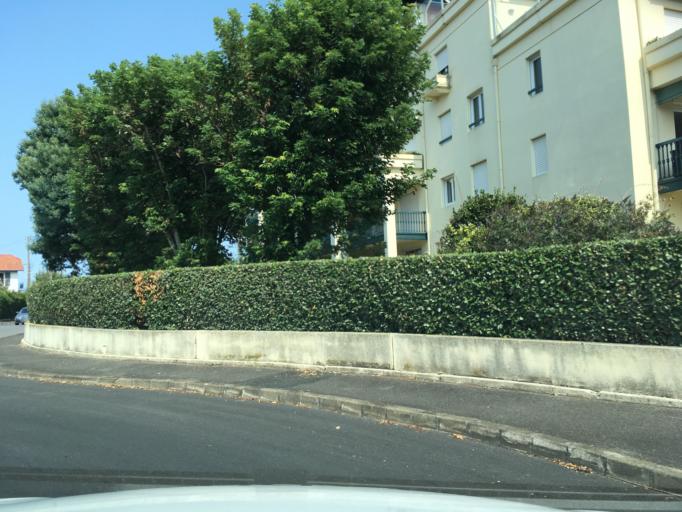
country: FR
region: Aquitaine
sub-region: Departement des Pyrenees-Atlantiques
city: Anglet
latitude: 43.4871
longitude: -1.5329
